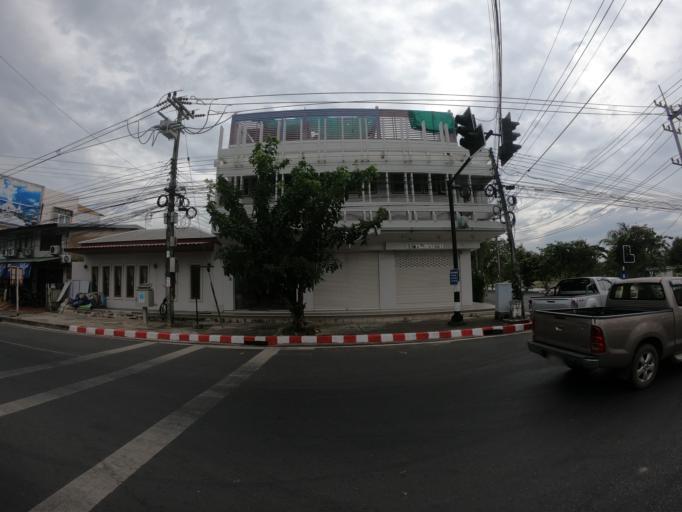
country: TH
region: Roi Et
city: Roi Et
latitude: 16.0614
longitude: 103.6599
